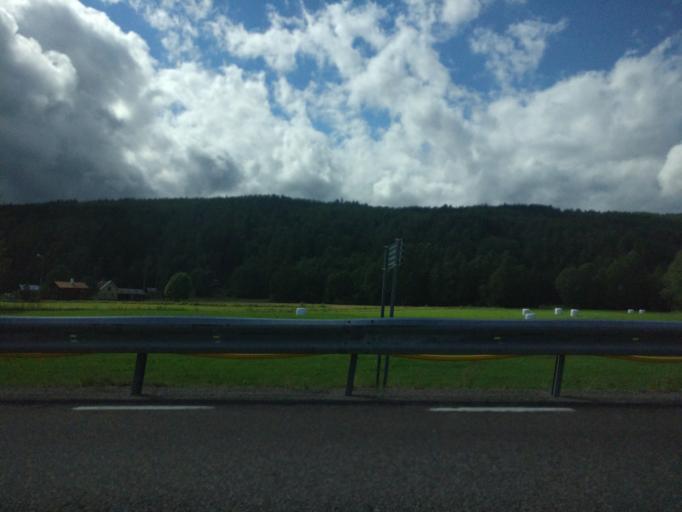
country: SE
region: Vaermland
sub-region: Hagfors Kommun
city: Ekshaerad
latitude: 60.2885
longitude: 13.3956
